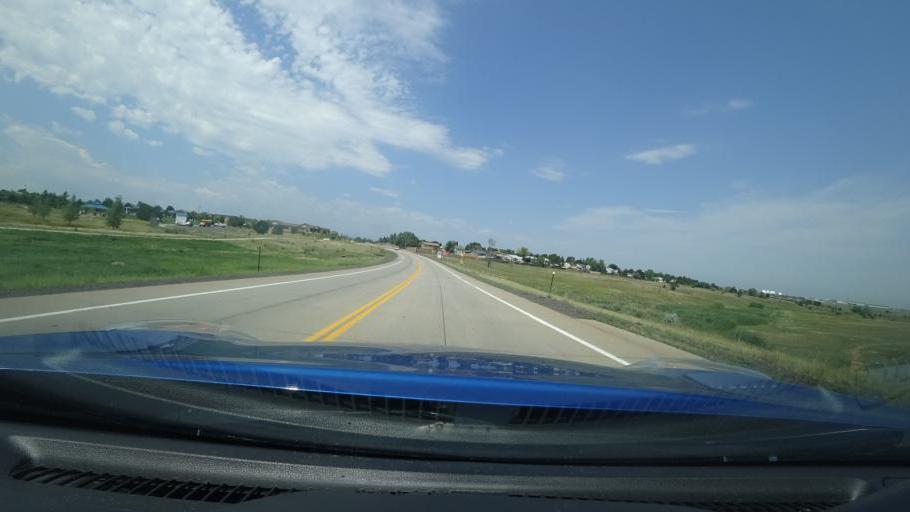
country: US
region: Colorado
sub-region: Adams County
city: Aurora
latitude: 39.6817
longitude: -104.7534
